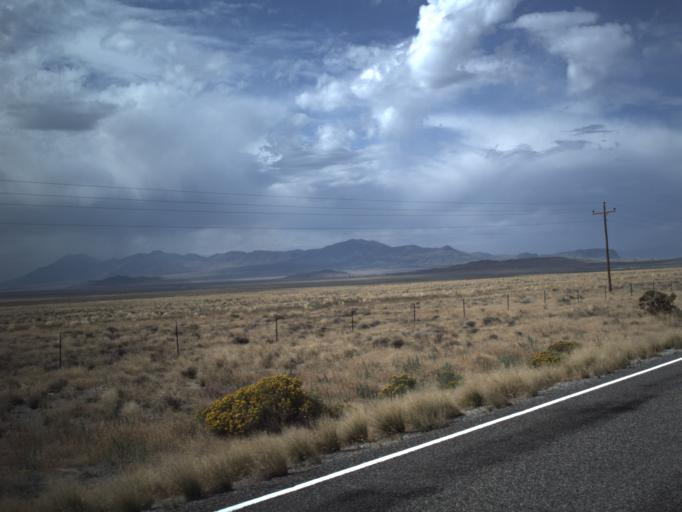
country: US
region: Utah
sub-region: Tooele County
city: Wendover
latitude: 41.4327
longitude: -113.7833
